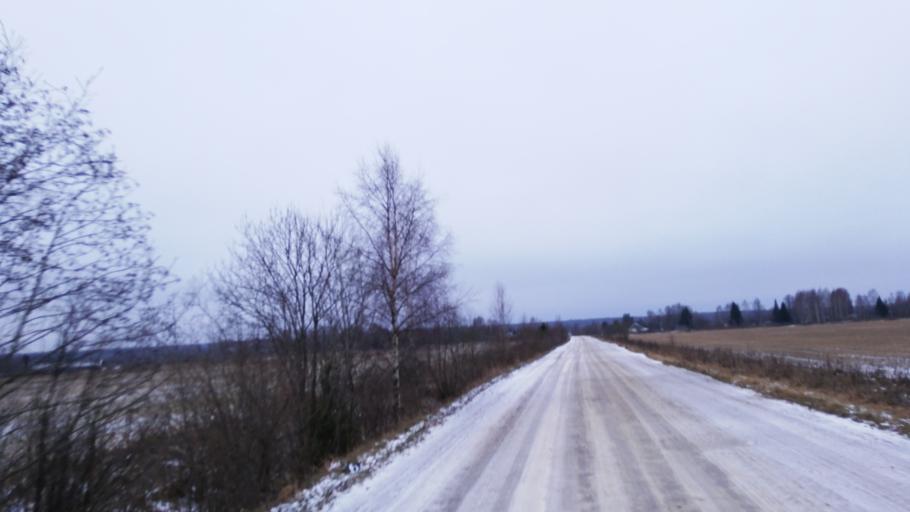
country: RU
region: Kostroma
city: Krasnoye-na-Volge
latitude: 57.6763
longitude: 41.1960
